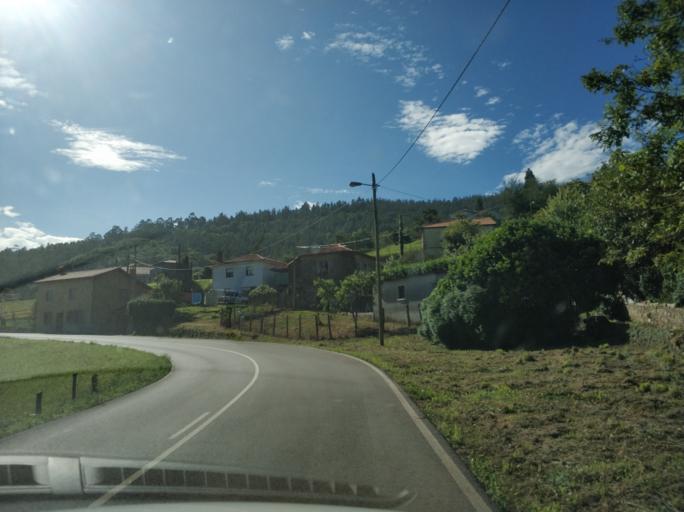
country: ES
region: Asturias
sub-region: Province of Asturias
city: Cudillero
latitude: 43.5409
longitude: -6.2317
